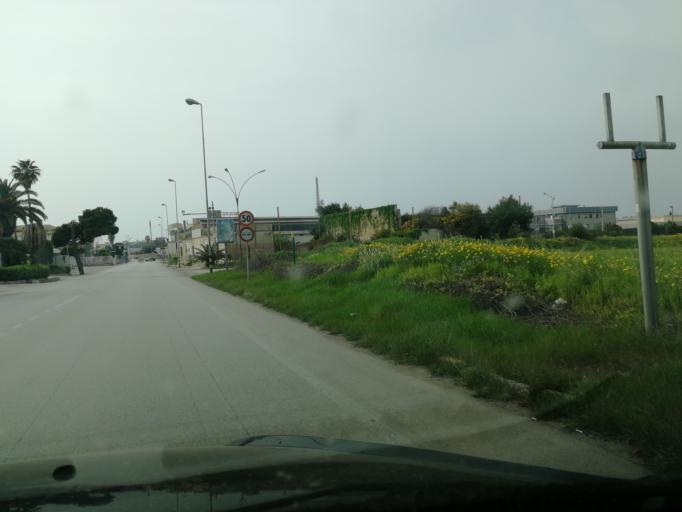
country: IT
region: Apulia
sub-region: Provincia di Barletta - Andria - Trani
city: Barletta
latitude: 41.3154
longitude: 16.3000
